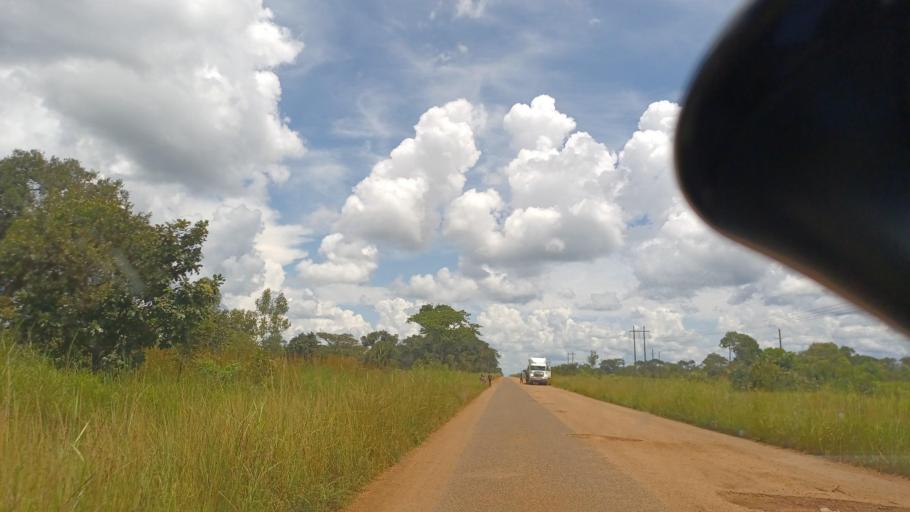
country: ZM
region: North-Western
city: Solwezi
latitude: -12.4904
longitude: 26.1903
